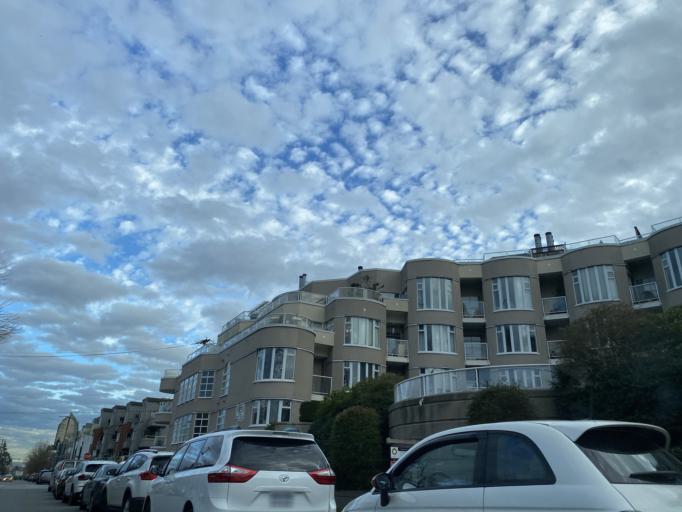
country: CA
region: British Columbia
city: West End
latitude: 49.2644
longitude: -123.1323
